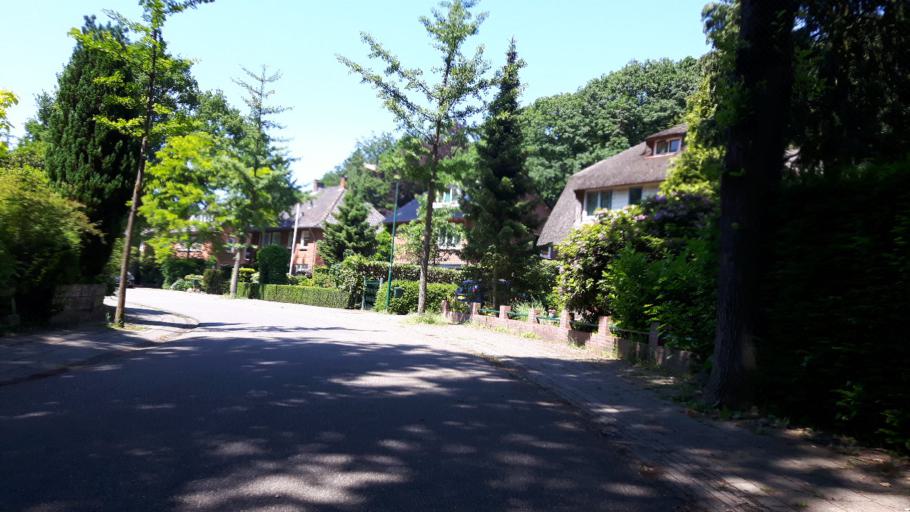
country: NL
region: Utrecht
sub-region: Gemeente Soest
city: Soest
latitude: 52.1588
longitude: 5.3142
